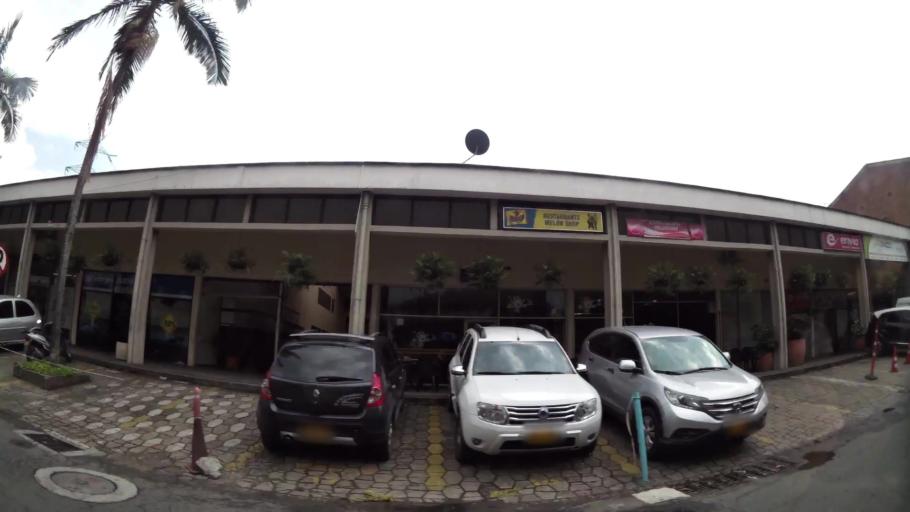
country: CO
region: Antioquia
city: Envigado
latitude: 6.1795
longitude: -75.5936
